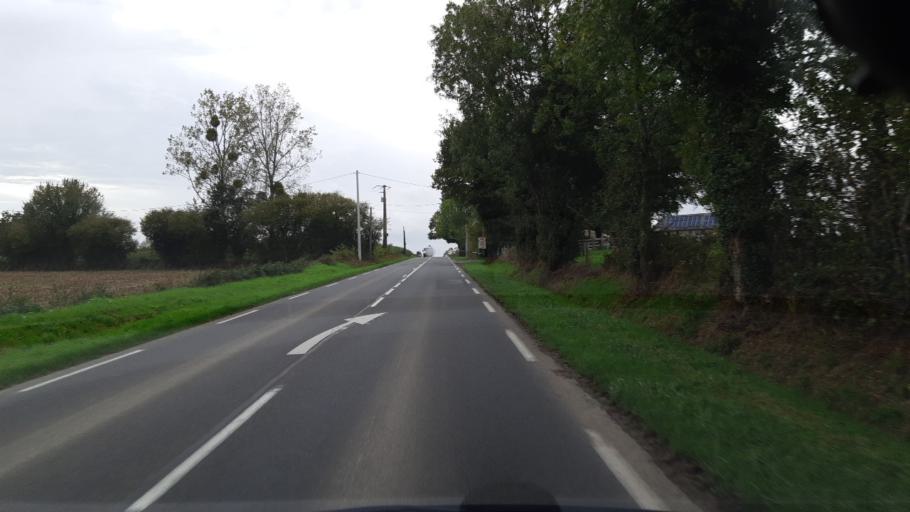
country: FR
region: Lower Normandy
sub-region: Departement de la Manche
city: Hambye
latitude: 48.9447
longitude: -1.2932
